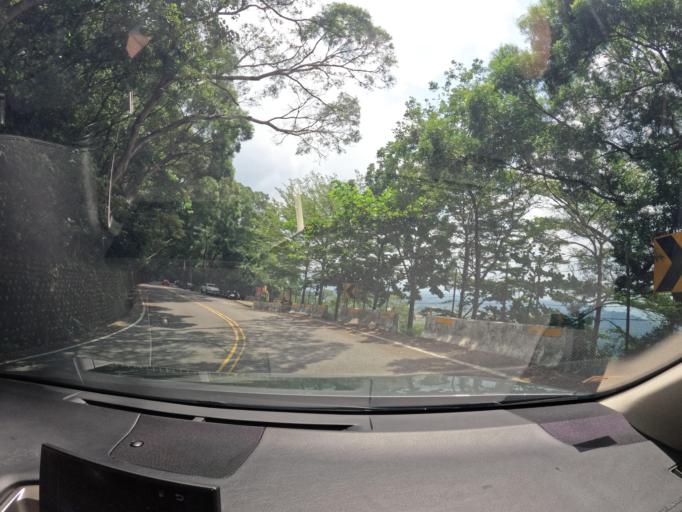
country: TW
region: Taiwan
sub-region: Nantou
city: Nantou
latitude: 23.8891
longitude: 120.6266
